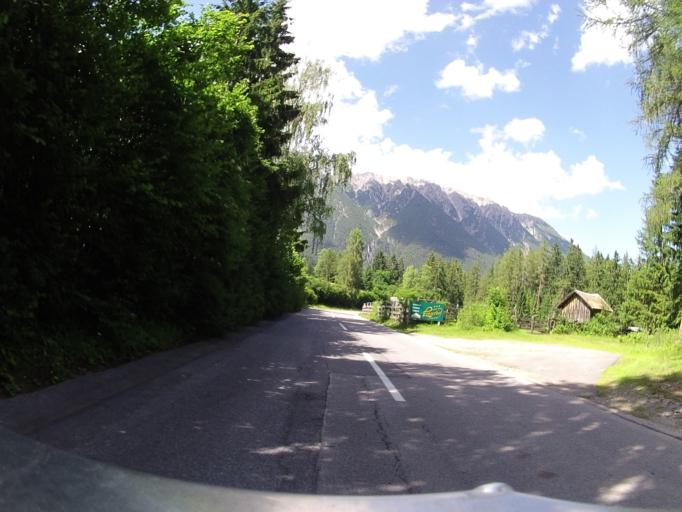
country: AT
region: Tyrol
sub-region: Politischer Bezirk Imst
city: Imst
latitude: 47.2641
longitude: 10.7404
